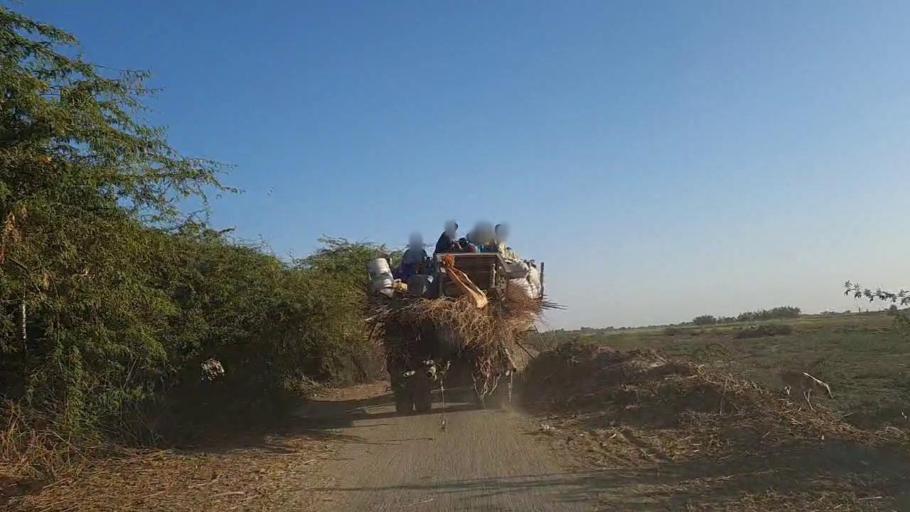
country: PK
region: Sindh
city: Naukot
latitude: 24.9891
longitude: 69.4031
